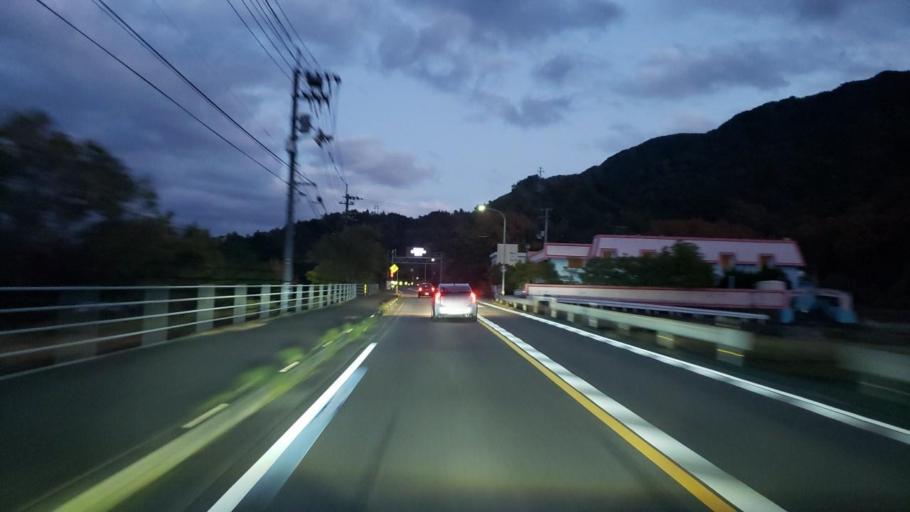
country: JP
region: Tokushima
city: Ishii
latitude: 34.2076
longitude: 134.4348
